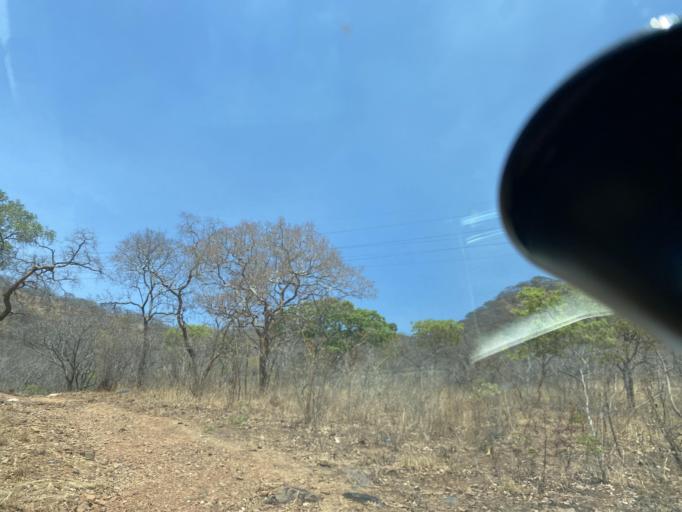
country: ZM
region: Lusaka
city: Kafue
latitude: -15.7437
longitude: 28.4713
